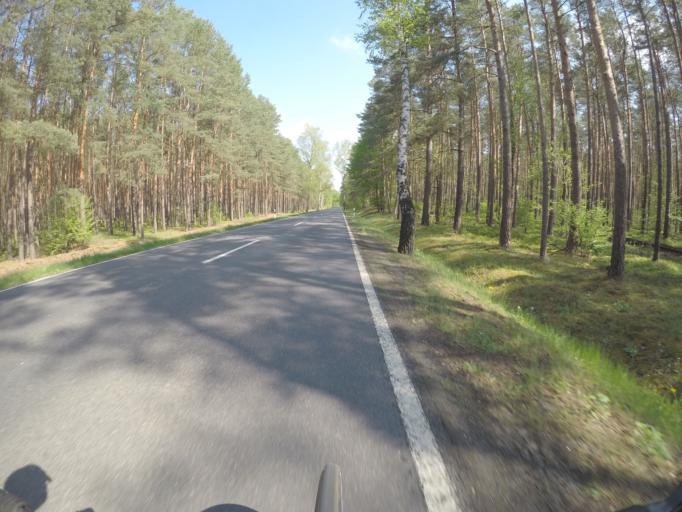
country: DE
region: Brandenburg
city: Marienwerder
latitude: 52.7997
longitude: 13.5511
